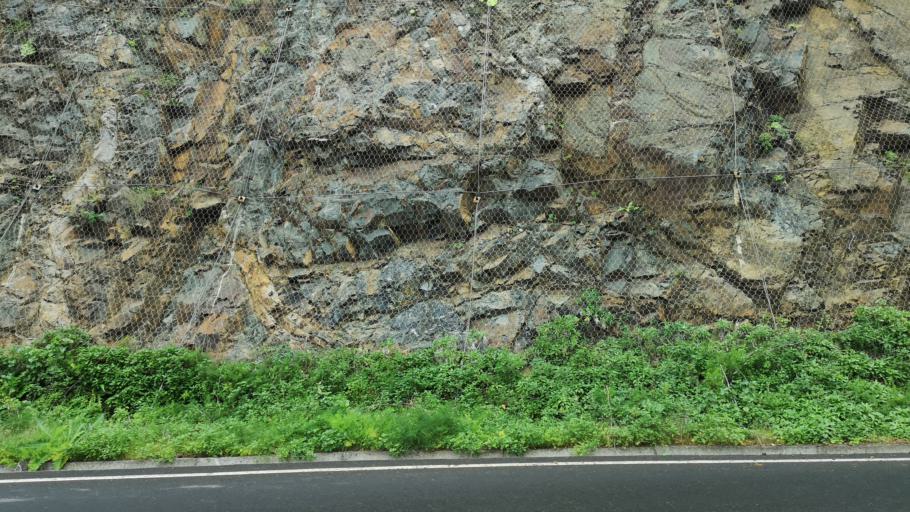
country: ES
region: Canary Islands
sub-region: Provincia de Santa Cruz de Tenerife
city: Agulo
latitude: 28.1882
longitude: -17.2166
